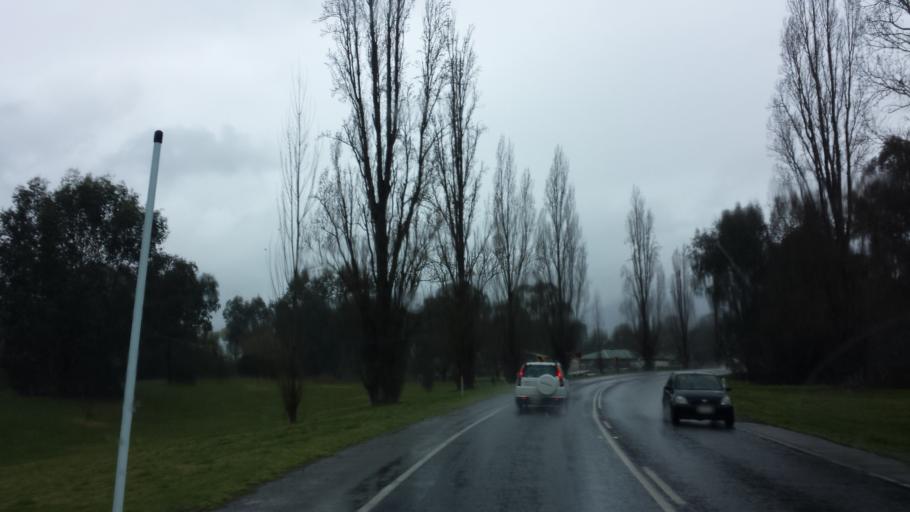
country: AU
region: Victoria
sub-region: Wangaratta
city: Wangaratta
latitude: -36.5520
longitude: 146.7077
